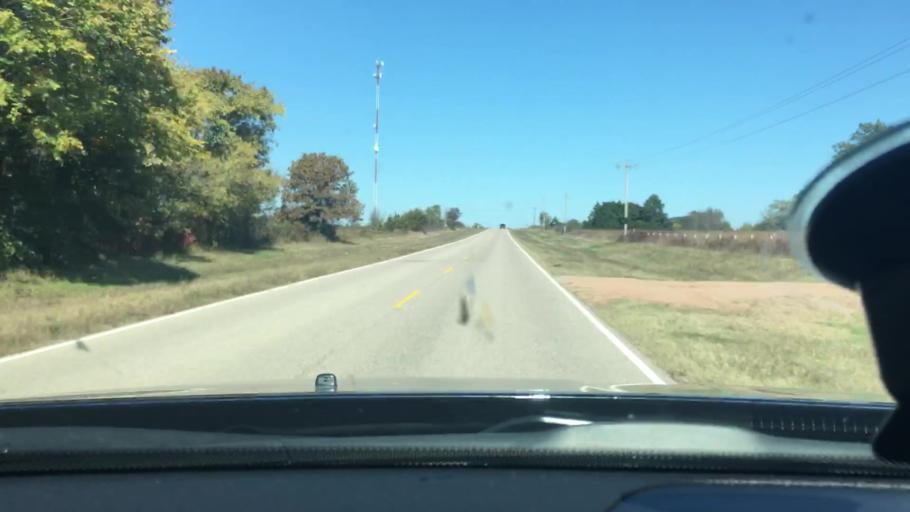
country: US
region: Oklahoma
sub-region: Johnston County
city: Tishomingo
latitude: 34.4278
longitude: -96.6363
